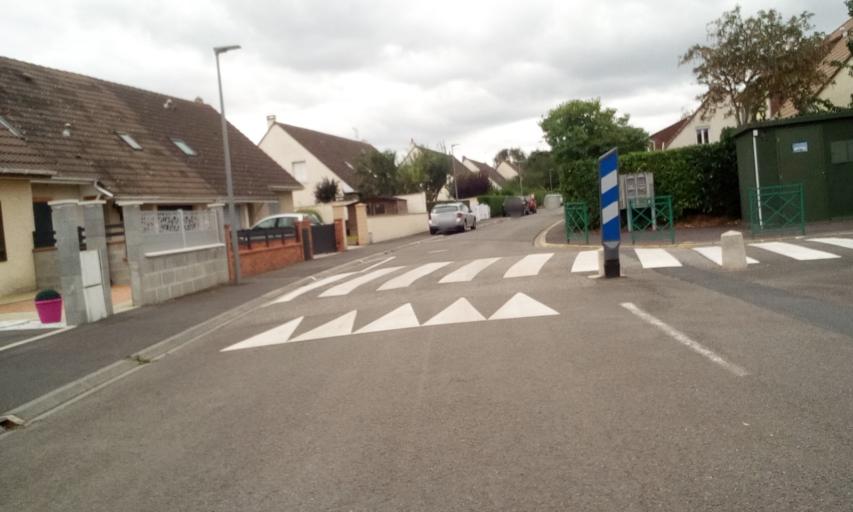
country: FR
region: Lower Normandy
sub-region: Departement du Calvados
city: Tourville-sur-Odon
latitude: 49.1400
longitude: -0.5019
